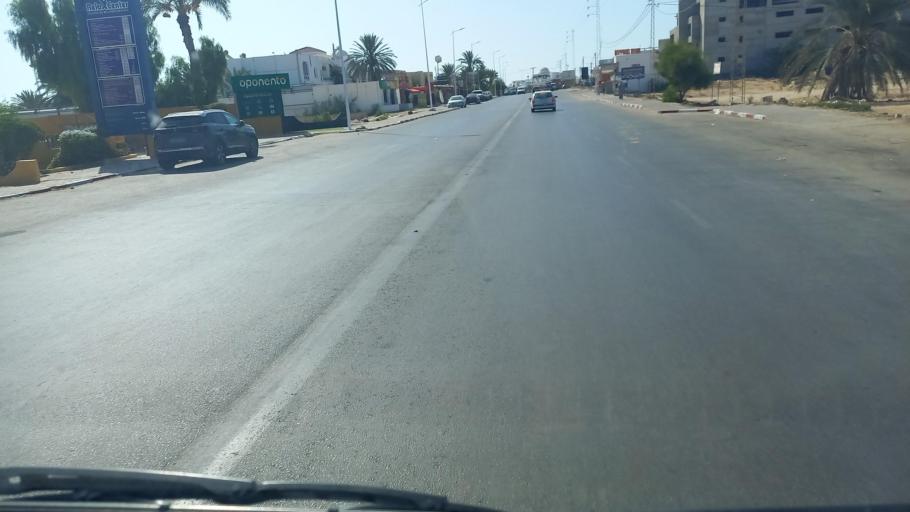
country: TN
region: Madanin
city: Midoun
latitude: 33.8413
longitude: 10.9908
